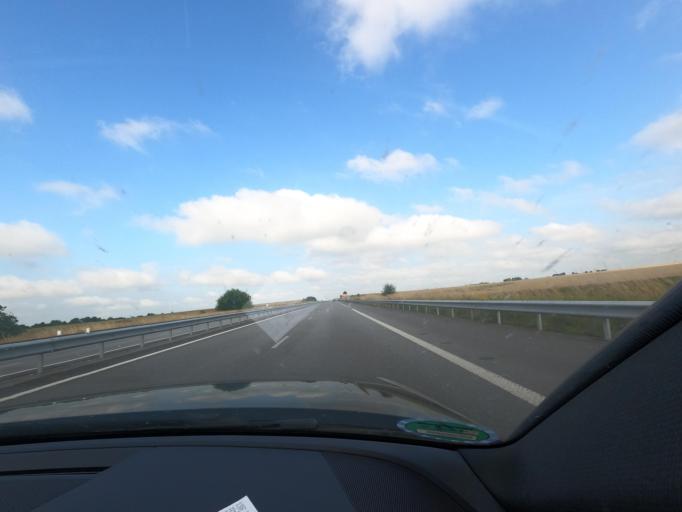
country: FR
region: Haute-Normandie
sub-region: Departement de la Seine-Maritime
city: Totes
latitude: 49.6441
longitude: 0.9928
